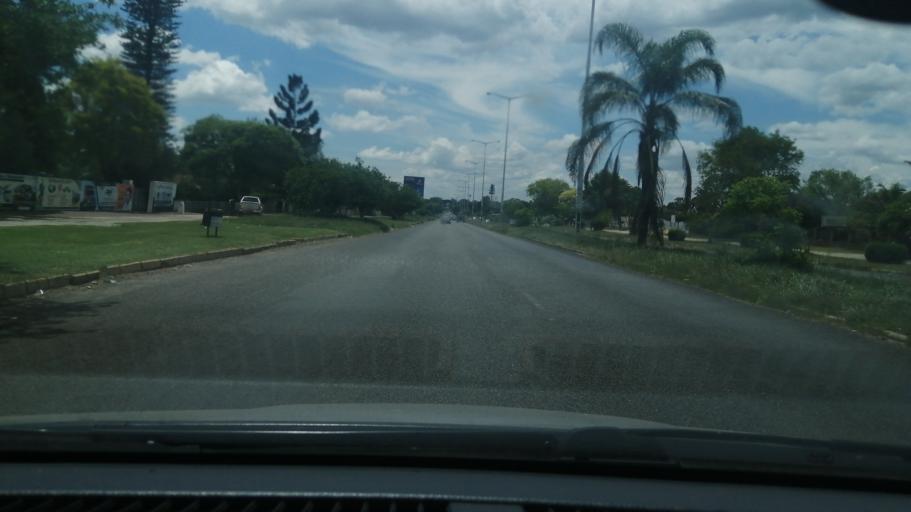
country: ZW
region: Harare
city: Harare
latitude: -17.8230
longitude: 31.0864
